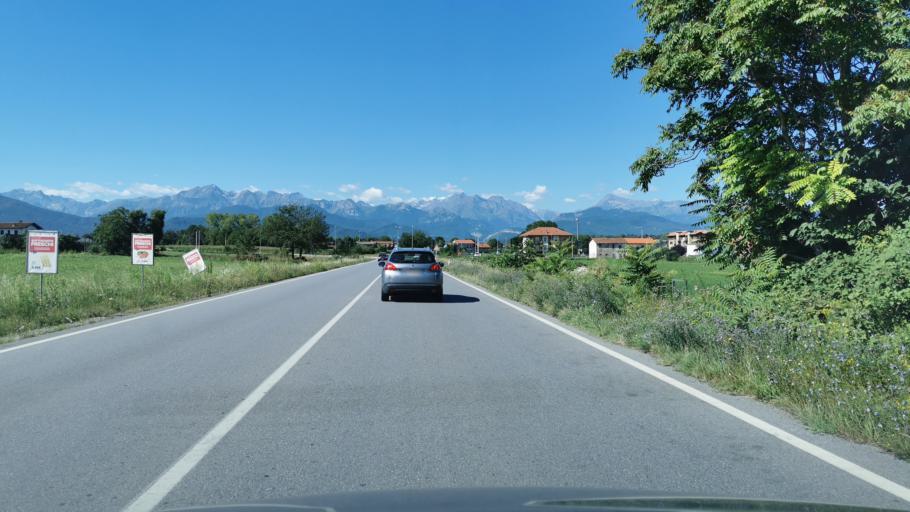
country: IT
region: Piedmont
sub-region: Provincia di Cuneo
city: Cuneo
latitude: 44.3862
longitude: 7.5684
